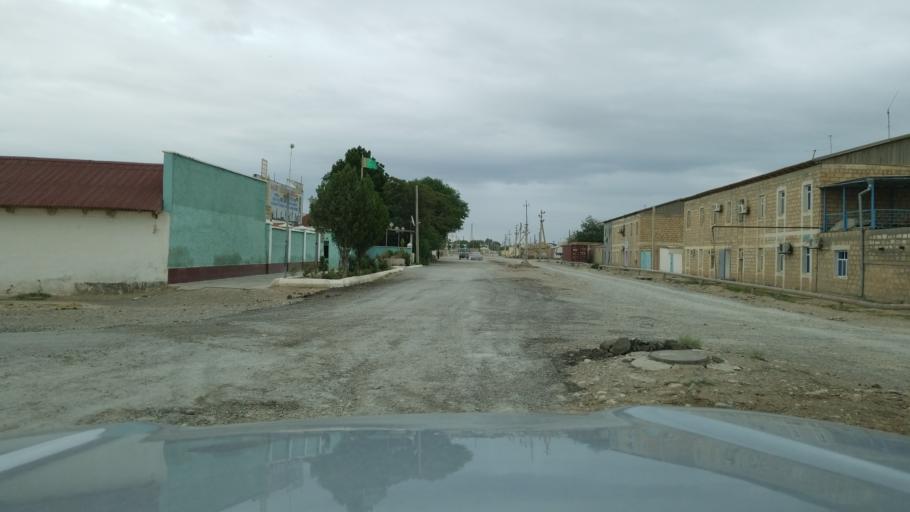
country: TM
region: Balkan
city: Serdar
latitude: 38.9852
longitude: 56.2567
